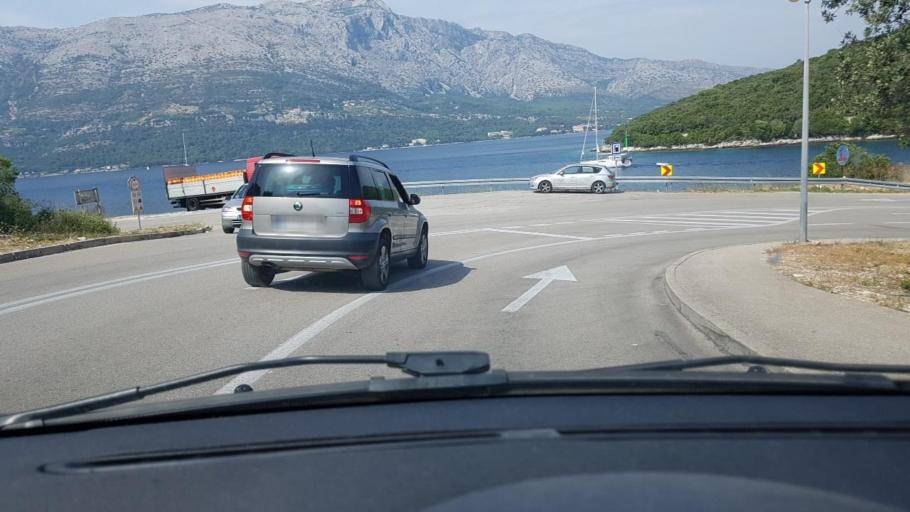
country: HR
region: Dubrovacko-Neretvanska
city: Korcula
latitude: 42.9534
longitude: 17.1490
